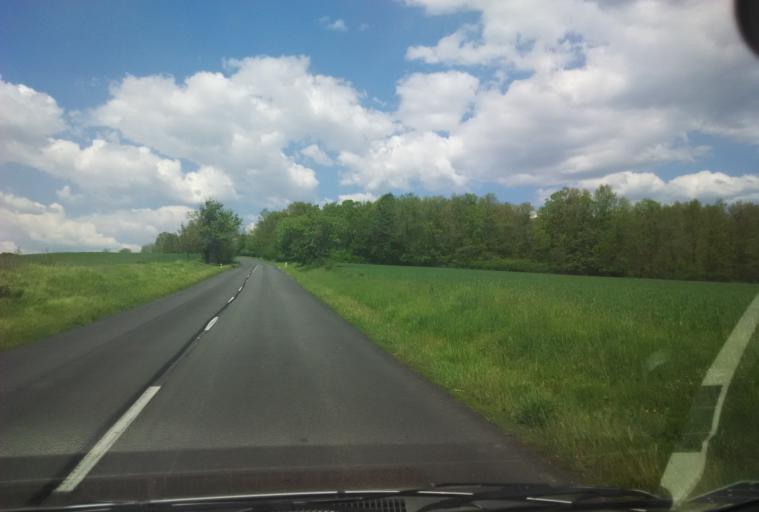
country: SK
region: Banskobystricky
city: Dudince
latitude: 48.2144
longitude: 18.7839
